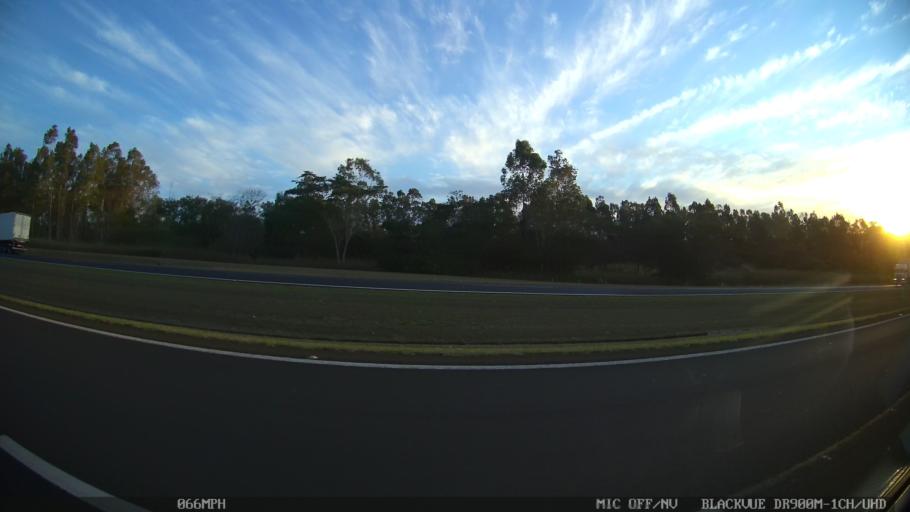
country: BR
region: Sao Paulo
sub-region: Pindorama
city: Pindorama
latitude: -21.2235
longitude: -48.9162
